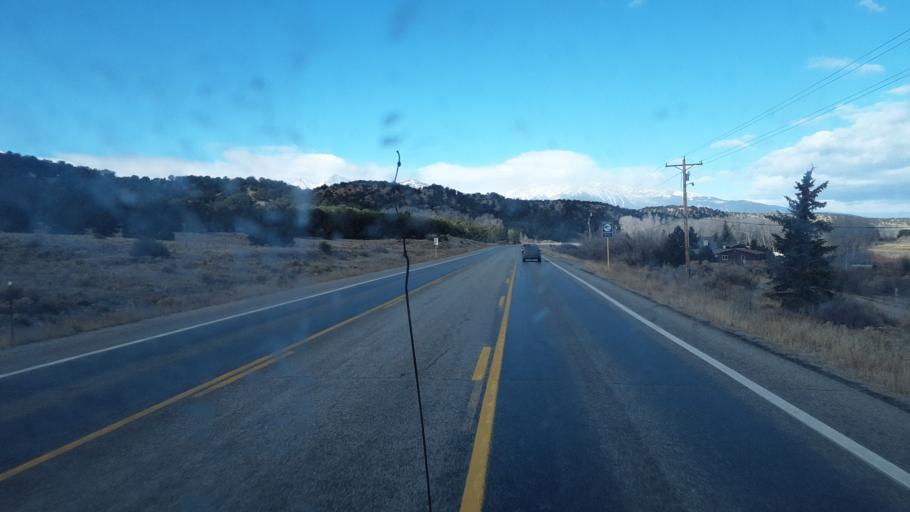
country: US
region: Colorado
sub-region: Chaffee County
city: Buena Vista
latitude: 38.7686
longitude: -106.1005
